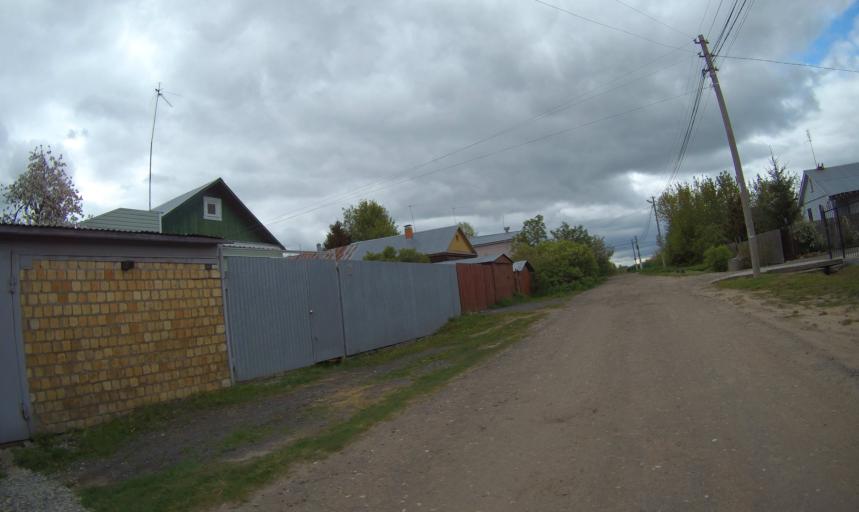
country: RU
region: Moskovskaya
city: Rechitsy
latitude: 55.5758
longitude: 38.4998
